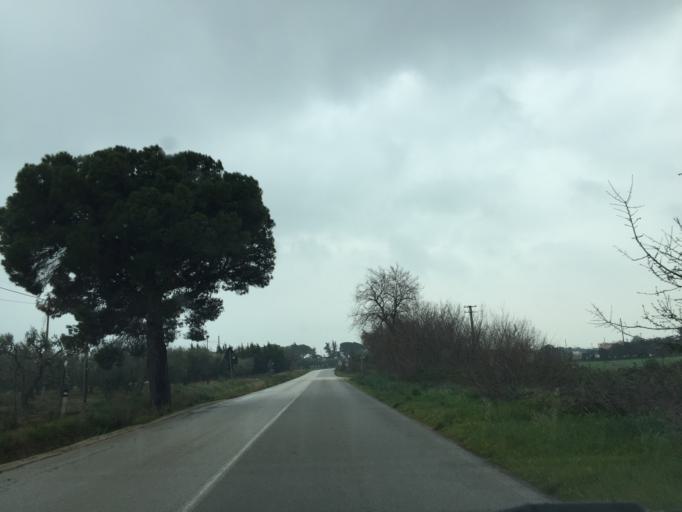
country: IT
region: Apulia
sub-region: Provincia di Foggia
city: Foggia
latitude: 41.4139
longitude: 15.4551
